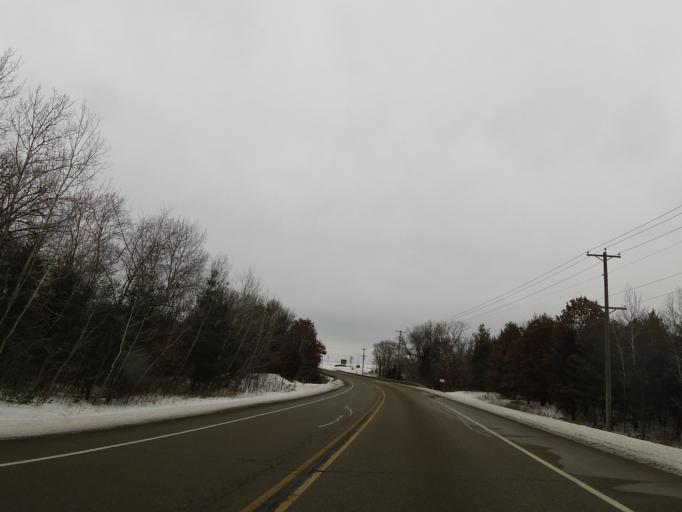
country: US
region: Minnesota
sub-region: Washington County
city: Bayport
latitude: 45.0405
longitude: -92.7555
